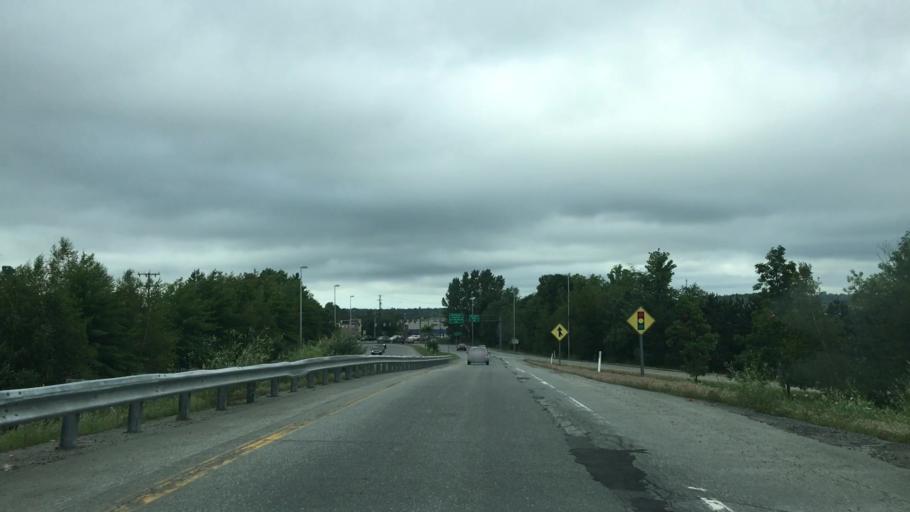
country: US
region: Maine
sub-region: Penobscot County
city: Brewer
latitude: 44.8263
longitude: -68.7543
